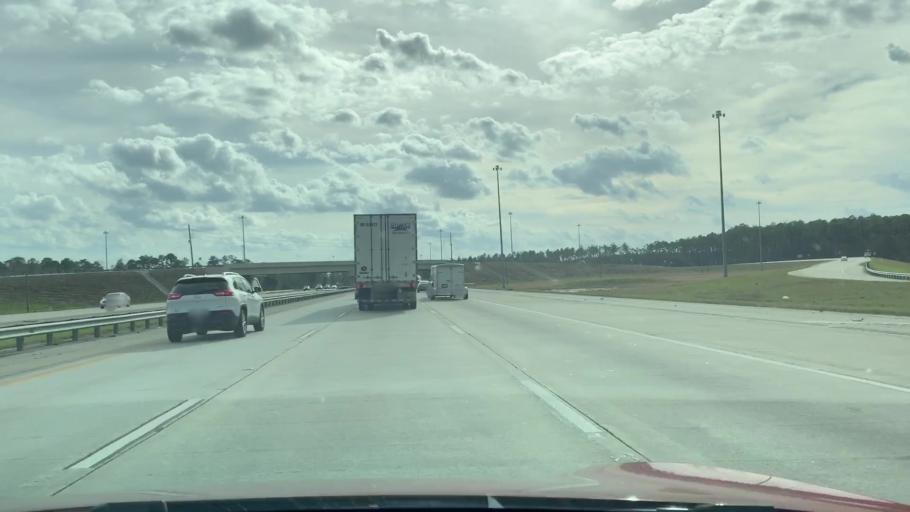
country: US
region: Georgia
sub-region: McIntosh County
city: Darien
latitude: 31.3083
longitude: -81.4795
